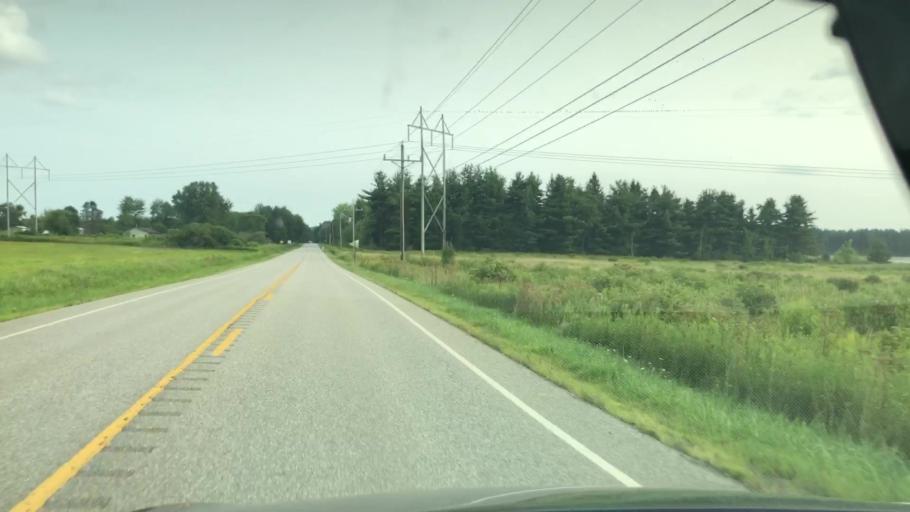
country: US
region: Pennsylvania
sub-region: Erie County
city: Union City
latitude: 41.9314
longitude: -79.8438
